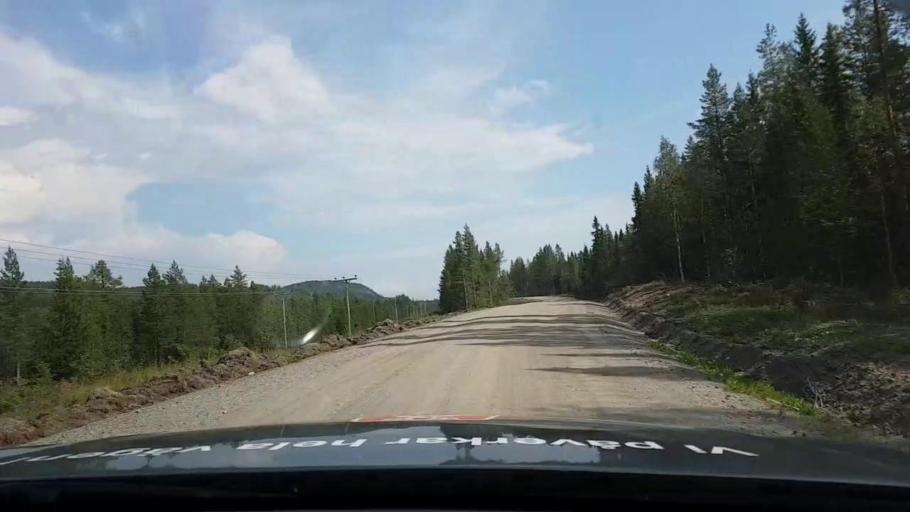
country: SE
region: Jaemtland
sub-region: Braecke Kommun
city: Braecke
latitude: 62.7261
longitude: 15.5038
